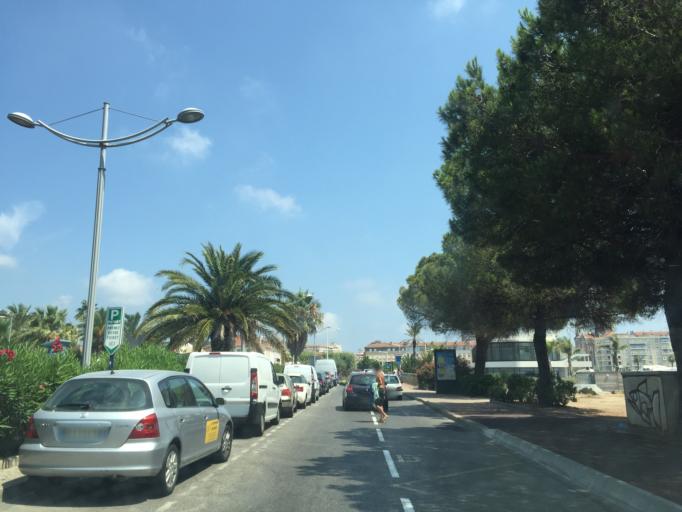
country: FR
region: Provence-Alpes-Cote d'Azur
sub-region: Departement du Var
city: Saint-Raphael
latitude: 43.4246
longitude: 6.7626
